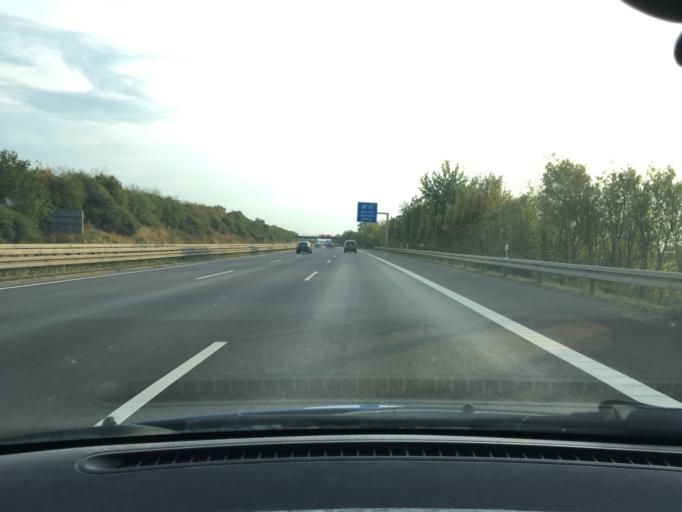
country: DE
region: Lower Saxony
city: Gross Munzel
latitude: 52.3971
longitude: 9.4881
